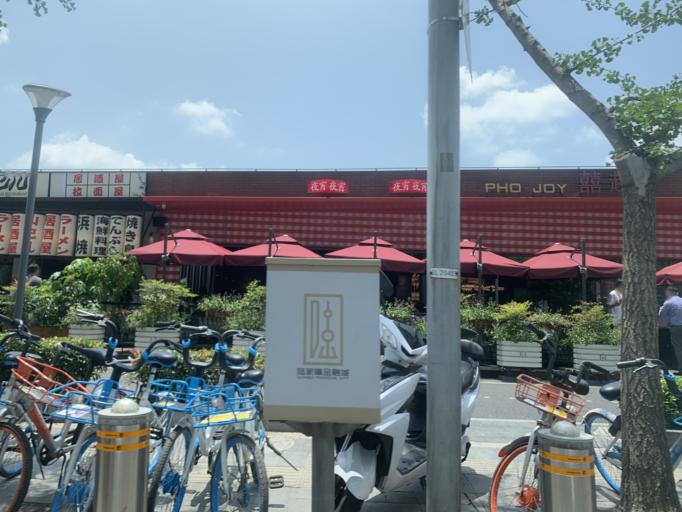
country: CN
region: Shanghai Shi
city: Hongkou
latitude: 31.2353
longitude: 121.4959
